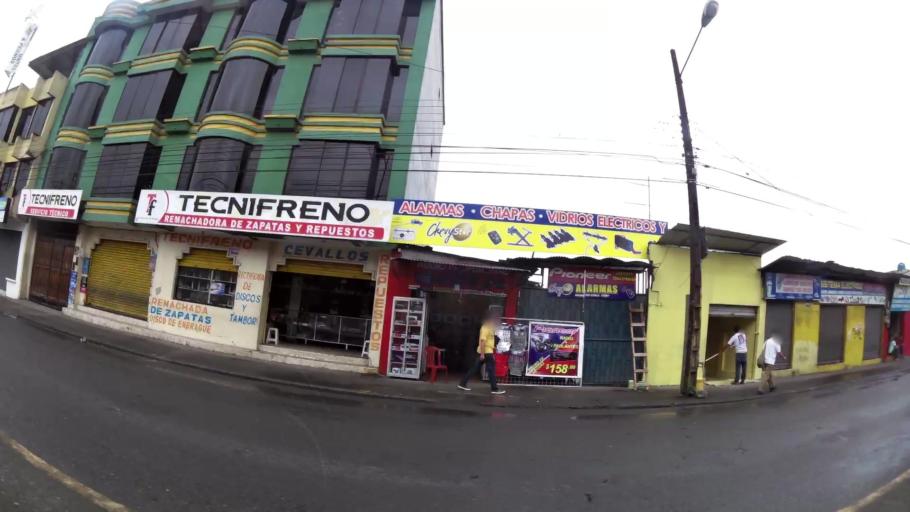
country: EC
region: Santo Domingo de los Tsachilas
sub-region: Canton Santo Domingo de los Colorados
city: Santo Domingo de los Colorados
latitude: -0.2570
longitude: -79.1784
